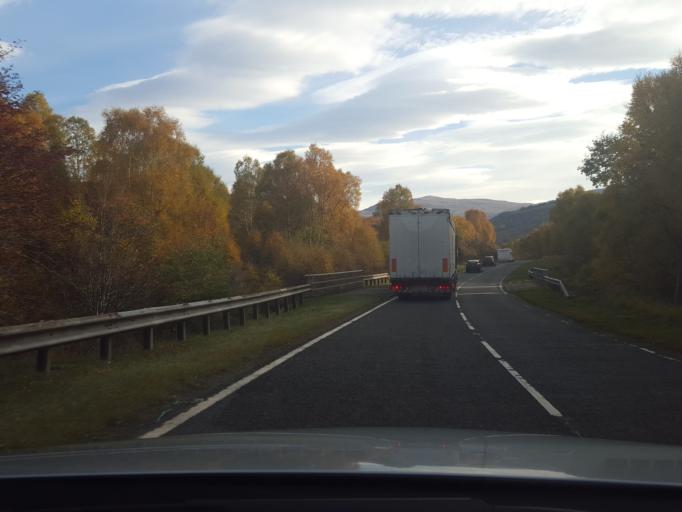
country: GB
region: Scotland
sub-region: Highland
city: Spean Bridge
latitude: 57.1456
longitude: -4.9879
